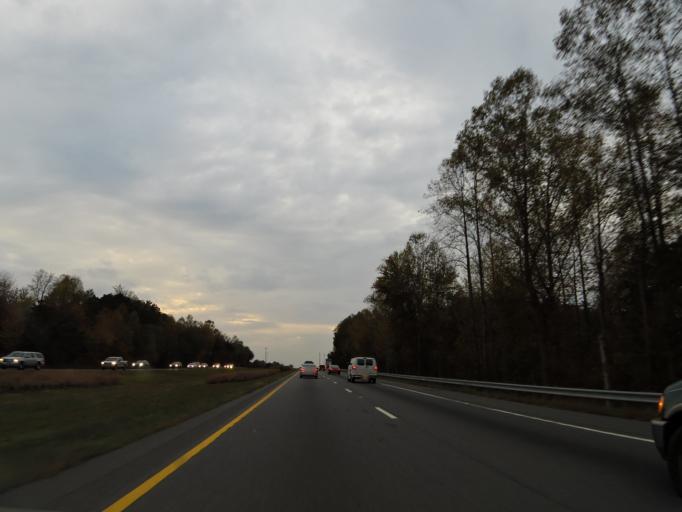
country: US
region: North Carolina
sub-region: Burke County
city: Hildebran
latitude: 35.7056
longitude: -81.4143
